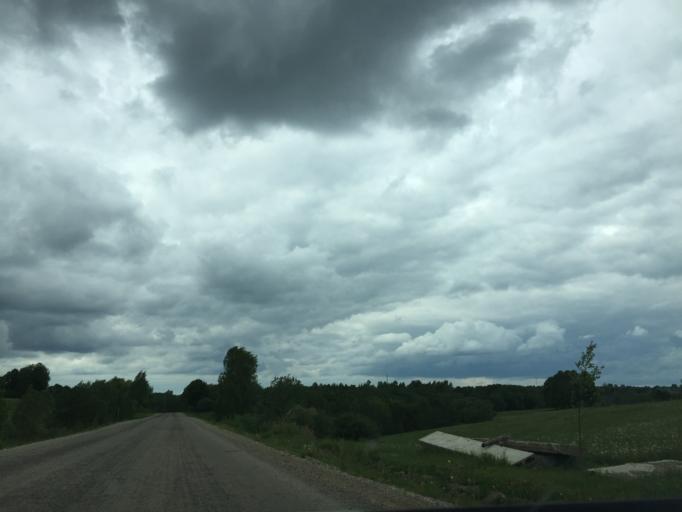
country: LV
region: Dagda
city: Dagda
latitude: 56.0782
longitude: 27.5394
